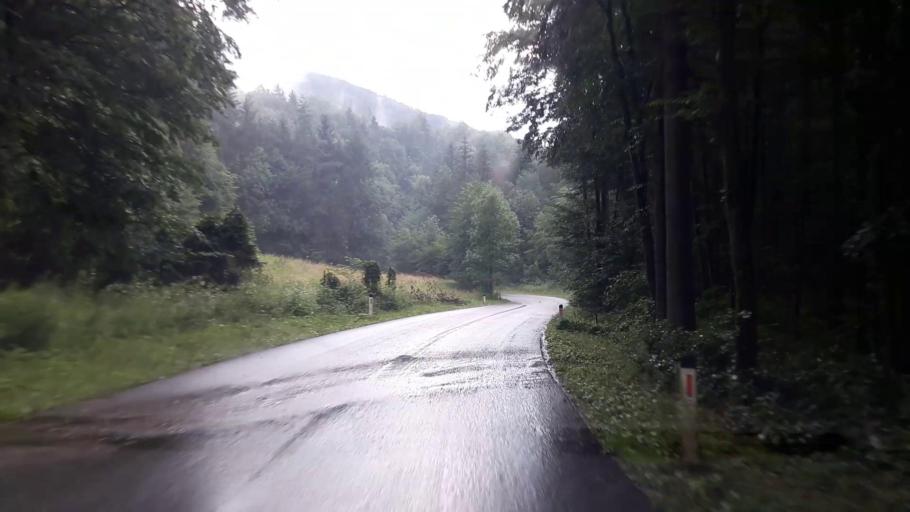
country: AT
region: Lower Austria
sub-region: Politischer Bezirk Krems
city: Aggsbach
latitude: 48.2896
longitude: 15.3910
